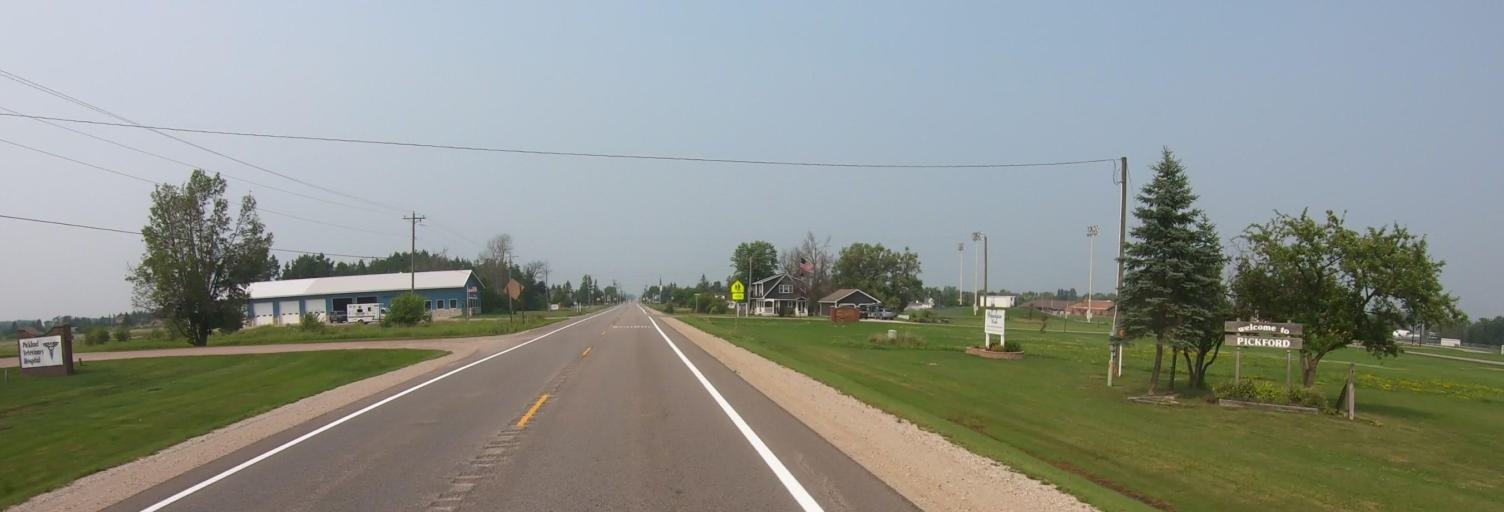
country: US
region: Michigan
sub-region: Chippewa County
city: Sault Ste. Marie
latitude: 46.1520
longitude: -84.3634
